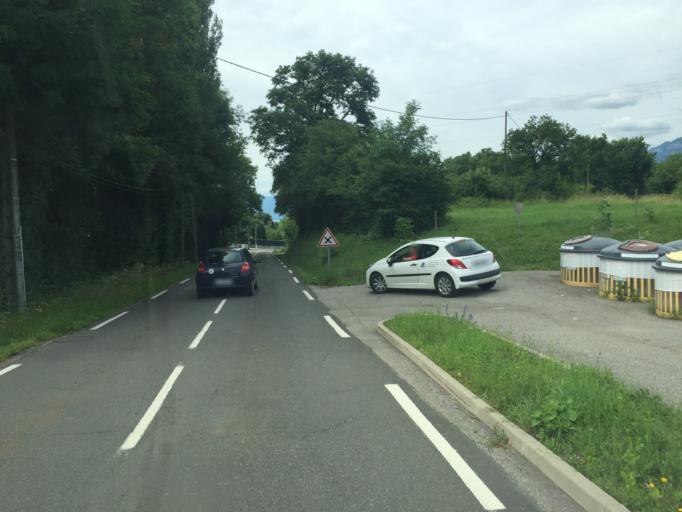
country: FR
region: Rhone-Alpes
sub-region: Departement de la Savoie
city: Jacob-Bellecombette
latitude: 45.5427
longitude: 5.9168
